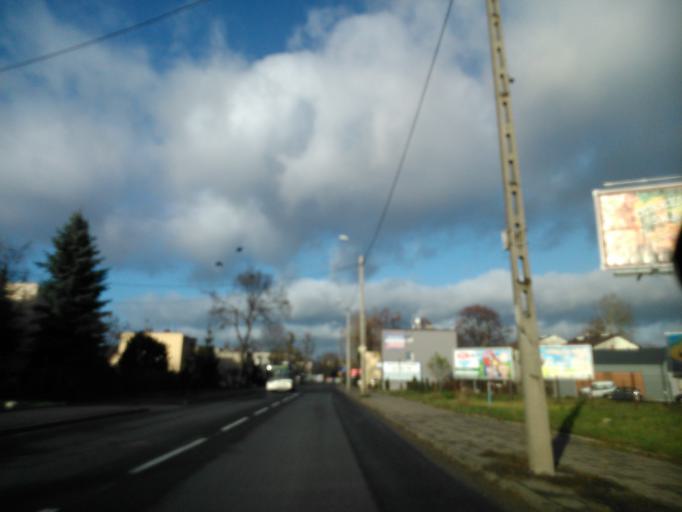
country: PL
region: Kujawsko-Pomorskie
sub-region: Torun
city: Torun
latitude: 52.9973
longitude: 18.6237
